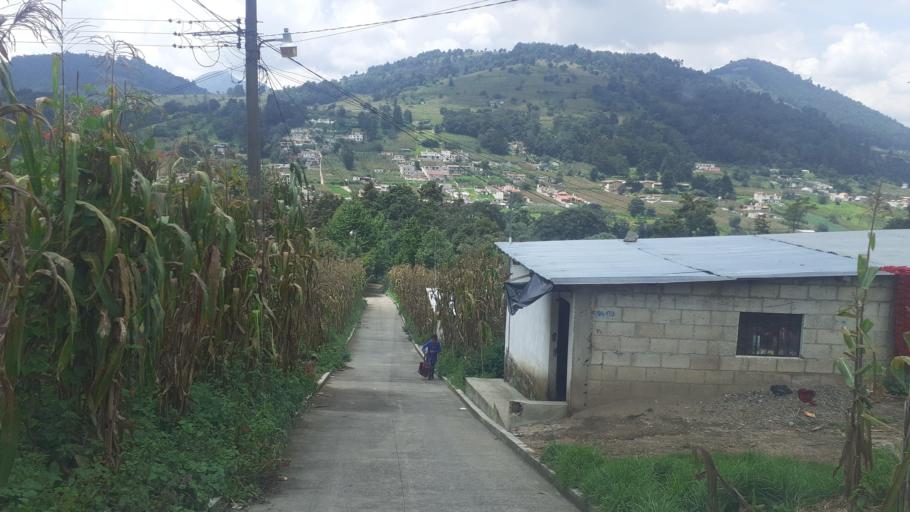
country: GT
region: Quetzaltenango
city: Cantel
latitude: 14.8191
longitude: -91.4504
